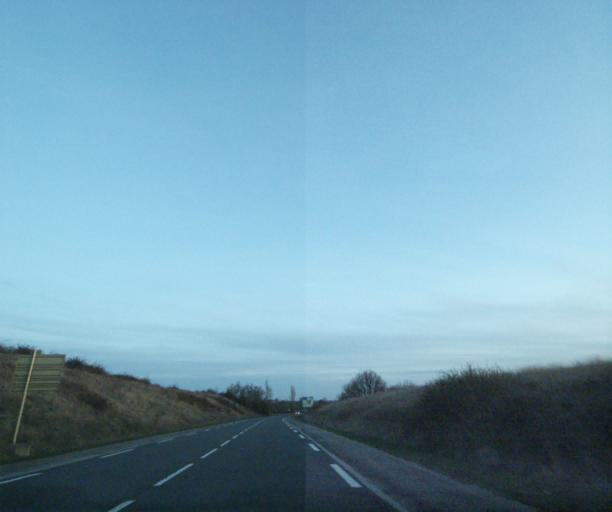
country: FR
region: Midi-Pyrenees
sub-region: Departement du Lot
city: Pradines
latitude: 44.5507
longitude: 1.4787
